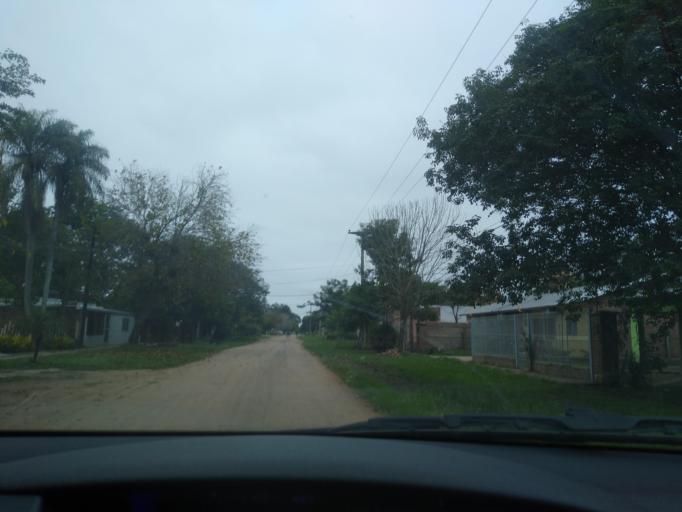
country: AR
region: Chaco
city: Colonia Benitez
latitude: -27.3315
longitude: -58.9417
